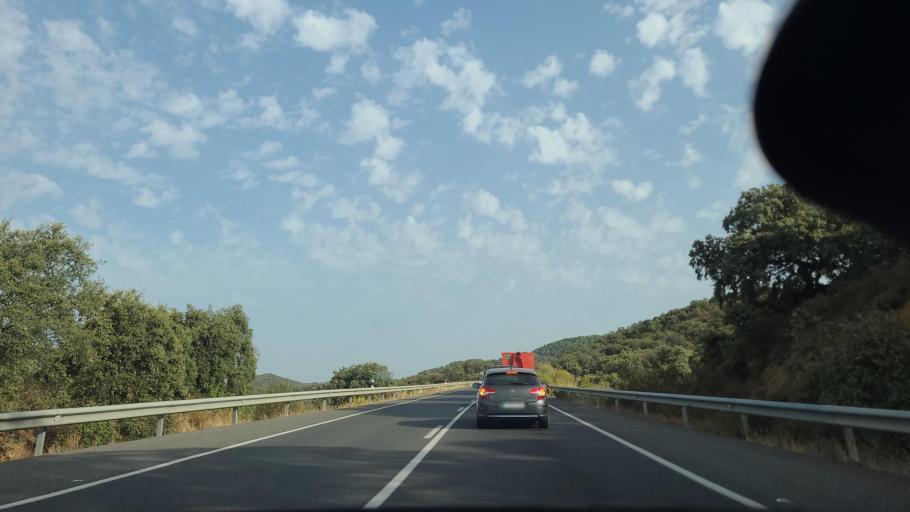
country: ES
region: Andalusia
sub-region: Province of Cordoba
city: Obejo
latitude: 38.0189
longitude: -4.8086
